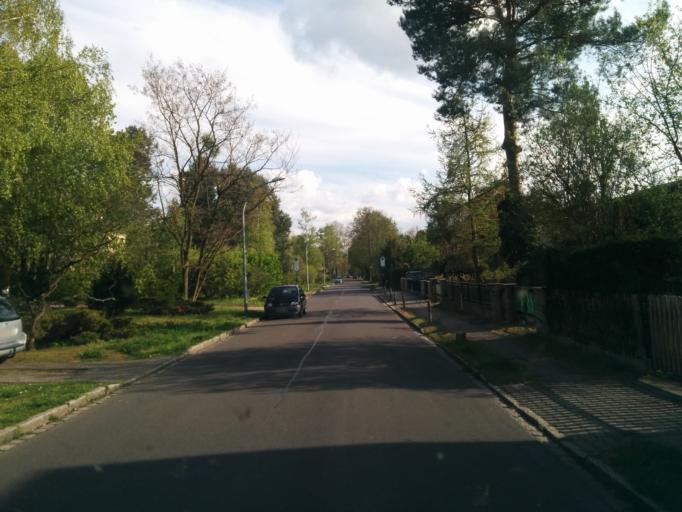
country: DE
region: Brandenburg
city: Kleinmachnow
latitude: 52.4054
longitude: 13.2054
